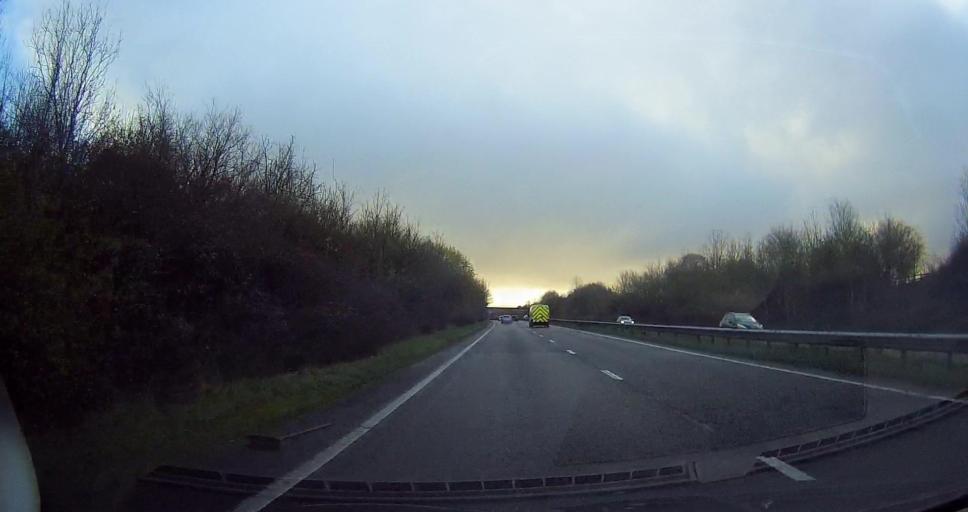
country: GB
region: England
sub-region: West Sussex
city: Hurstpierpoint
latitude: 50.9384
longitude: -0.1951
